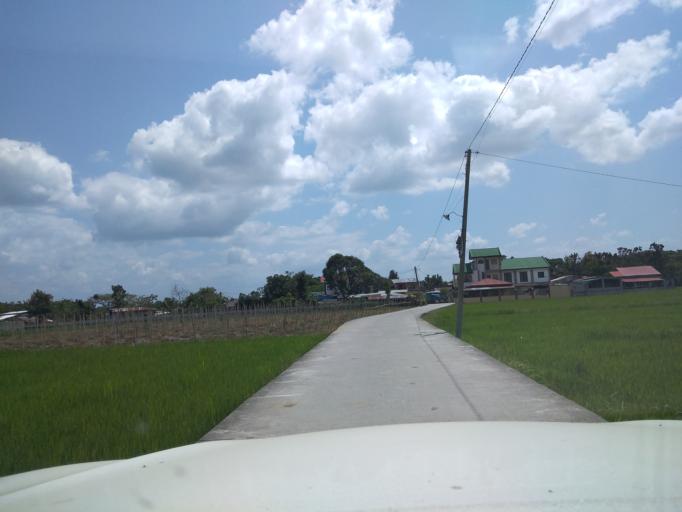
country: PH
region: Central Luzon
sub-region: Province of Pampanga
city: Bahay Pare
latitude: 15.0126
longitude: 120.8720
